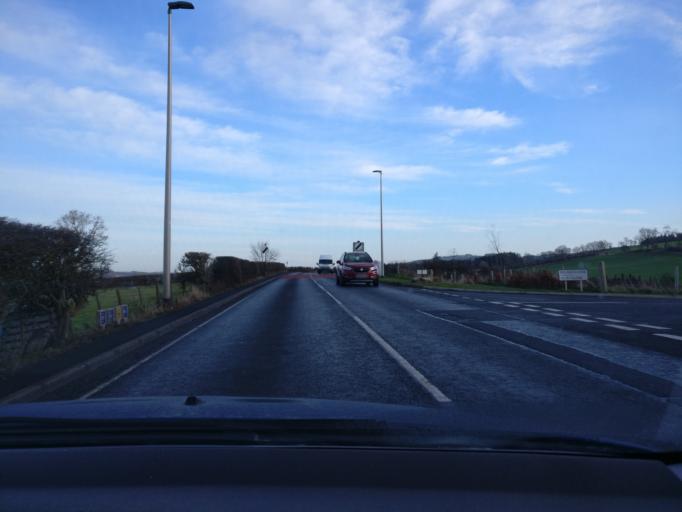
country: GB
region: Scotland
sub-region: The Scottish Borders
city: Hawick
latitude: 55.4593
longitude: -2.6787
